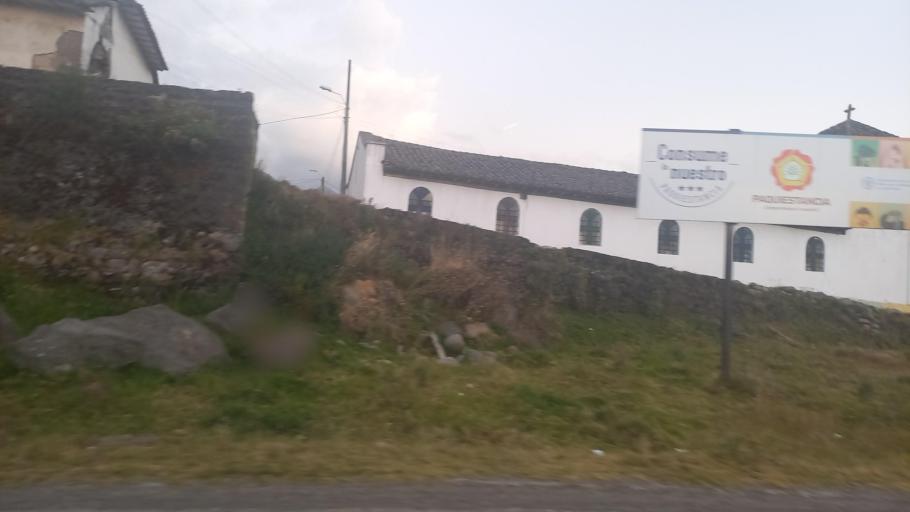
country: EC
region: Pichincha
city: Cayambe
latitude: 0.0713
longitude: -78.1103
